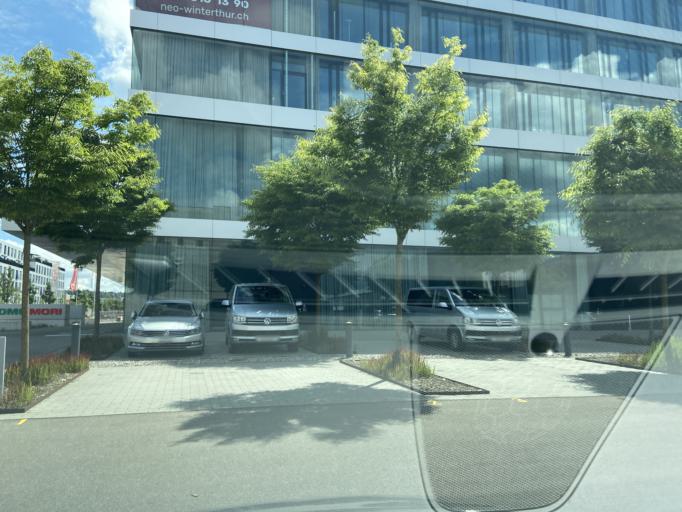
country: CH
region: Zurich
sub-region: Bezirk Winterthur
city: Oberwinterthur (Kreis 2) / Hegi
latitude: 47.5022
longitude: 8.7643
